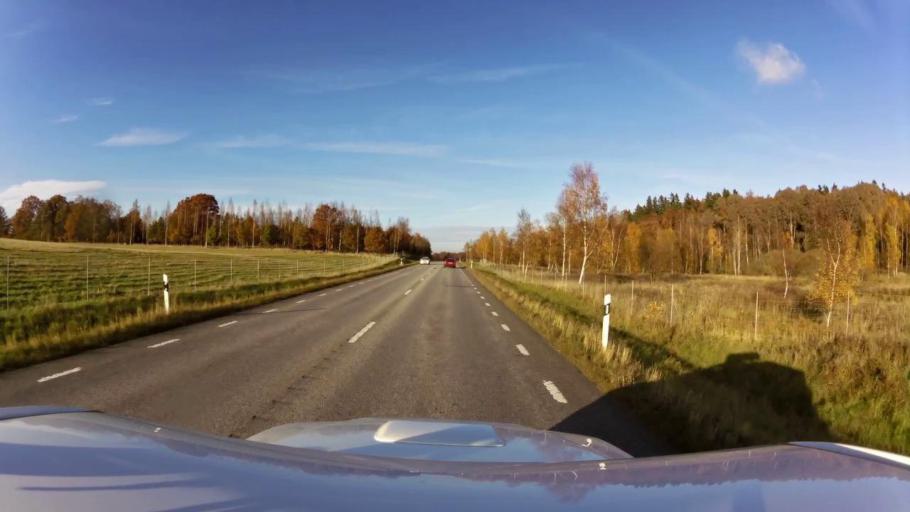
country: SE
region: OEstergoetland
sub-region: Kinda Kommun
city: Rimforsa
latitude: 58.2030
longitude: 15.6683
